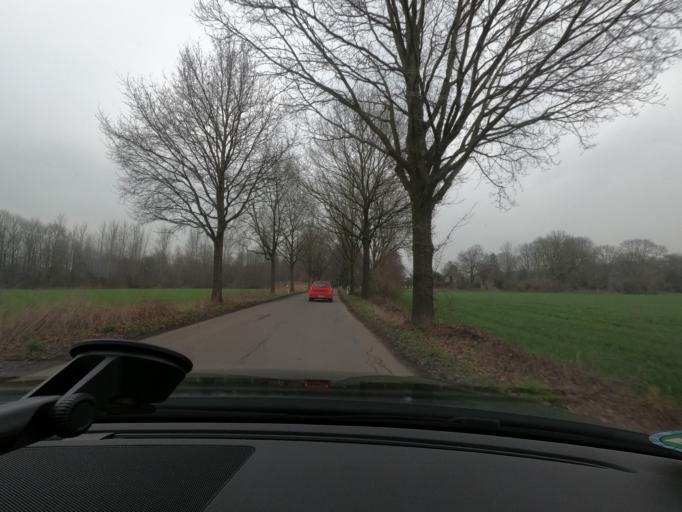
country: DE
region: North Rhine-Westphalia
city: Tonisvorst
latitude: 51.3882
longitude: 6.5119
